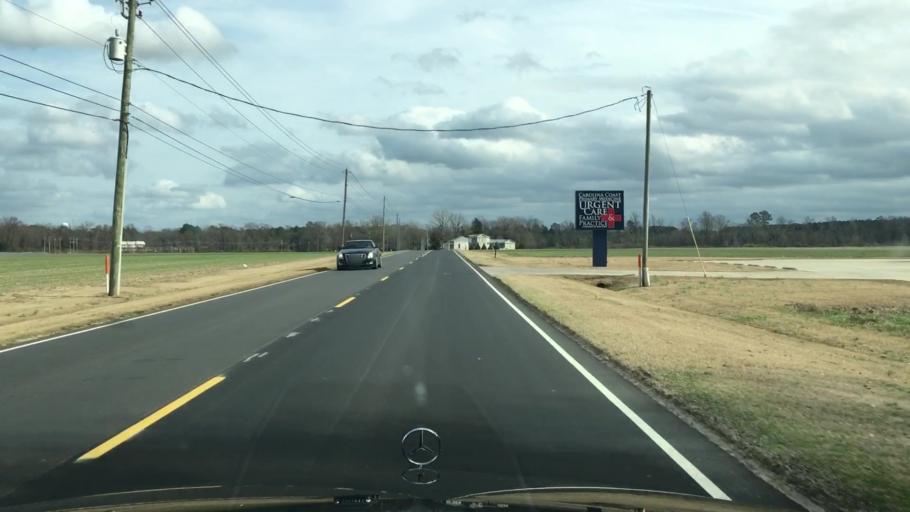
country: US
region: North Carolina
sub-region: Duplin County
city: Kenansville
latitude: 34.9594
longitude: -77.9860
